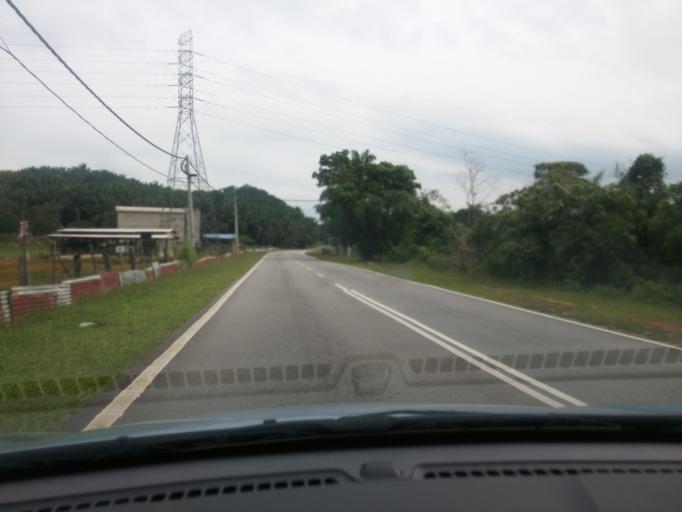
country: MY
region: Pahang
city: Kuantan
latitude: 3.8791
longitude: 103.1735
